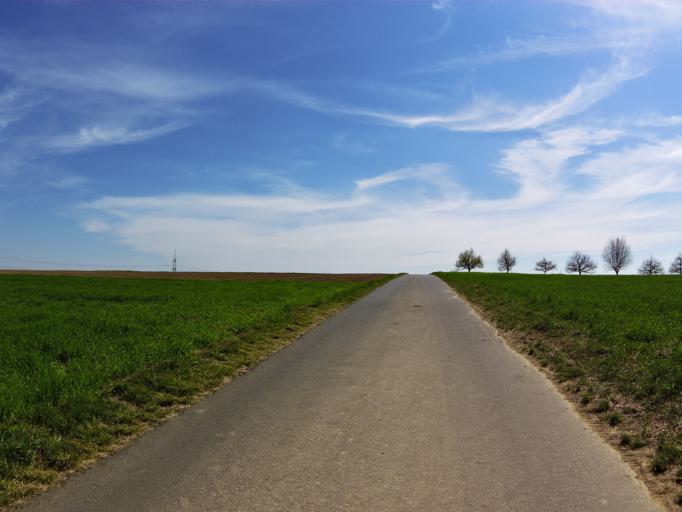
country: DE
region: Bavaria
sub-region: Regierungsbezirk Unterfranken
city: Rottendorf
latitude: 49.7954
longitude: 10.0498
